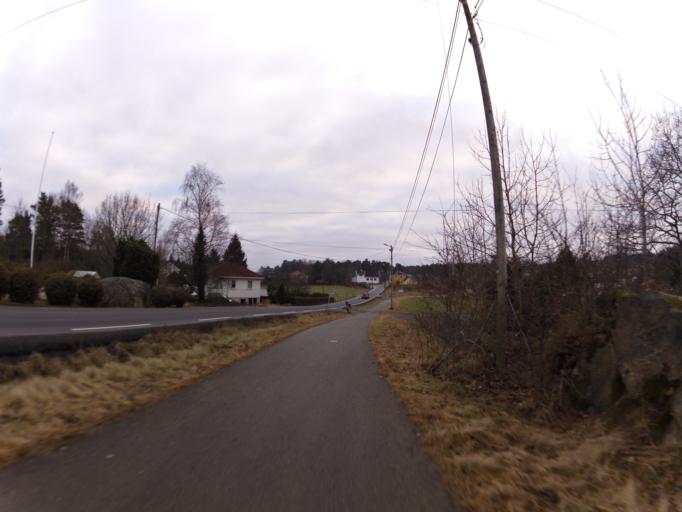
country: NO
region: Ostfold
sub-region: Fredrikstad
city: Fredrikstad
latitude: 59.1911
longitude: 10.8784
